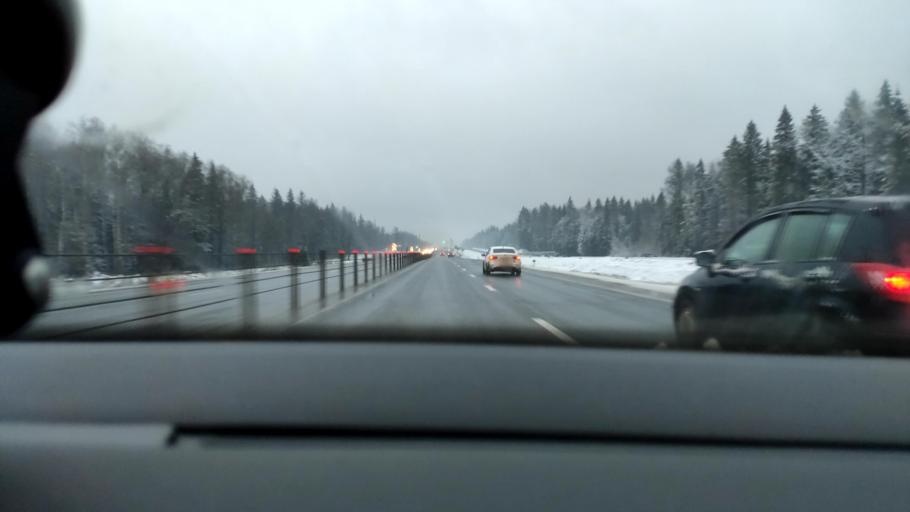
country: RU
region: Moskovskaya
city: Kubinka
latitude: 55.5777
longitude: 36.7608
